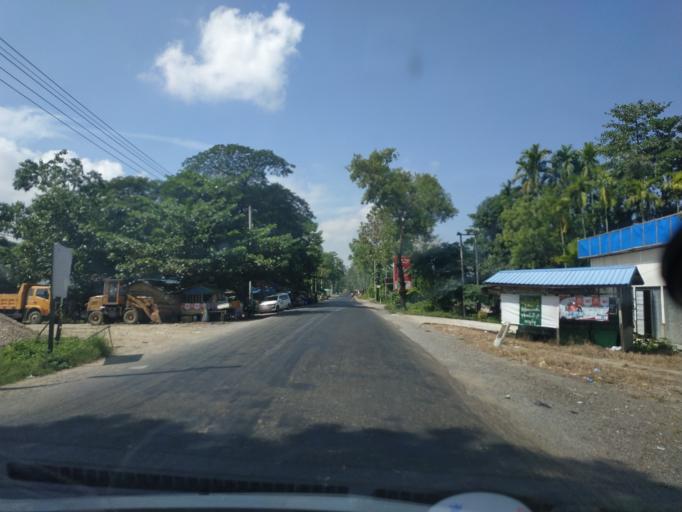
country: MM
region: Ayeyarwady
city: Nyaungdon
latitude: 17.0465
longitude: 95.5484
